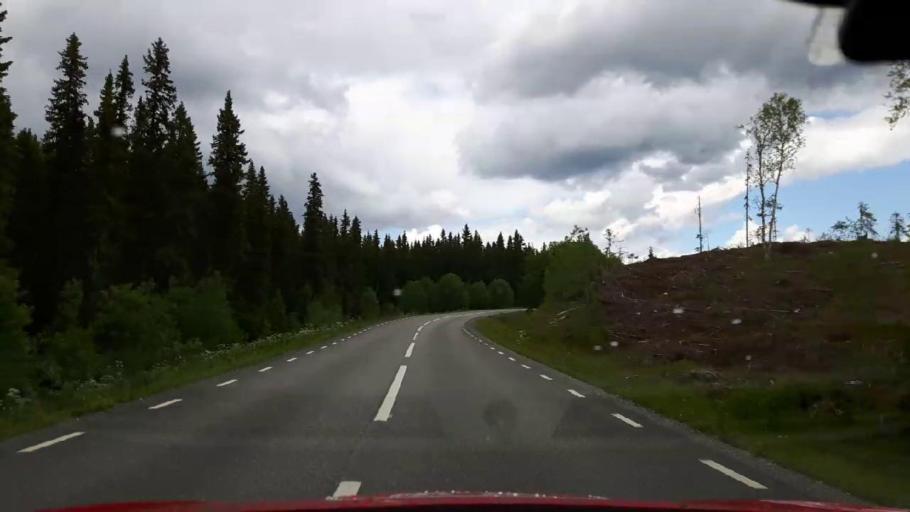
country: SE
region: Jaemtland
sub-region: Krokoms Kommun
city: Krokom
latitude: 63.7802
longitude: 14.3500
